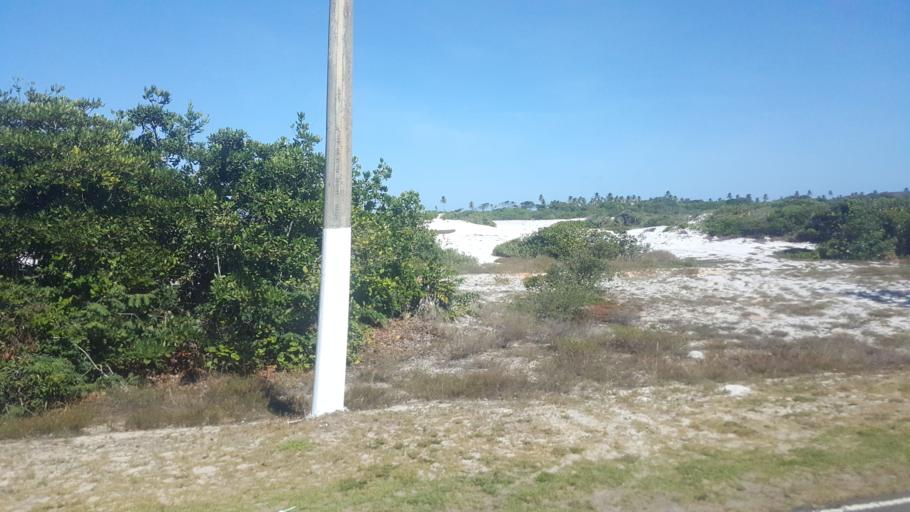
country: BR
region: Bahia
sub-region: Mata De Sao Joao
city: Mata de Sao Joao
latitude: -12.4322
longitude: -37.9197
